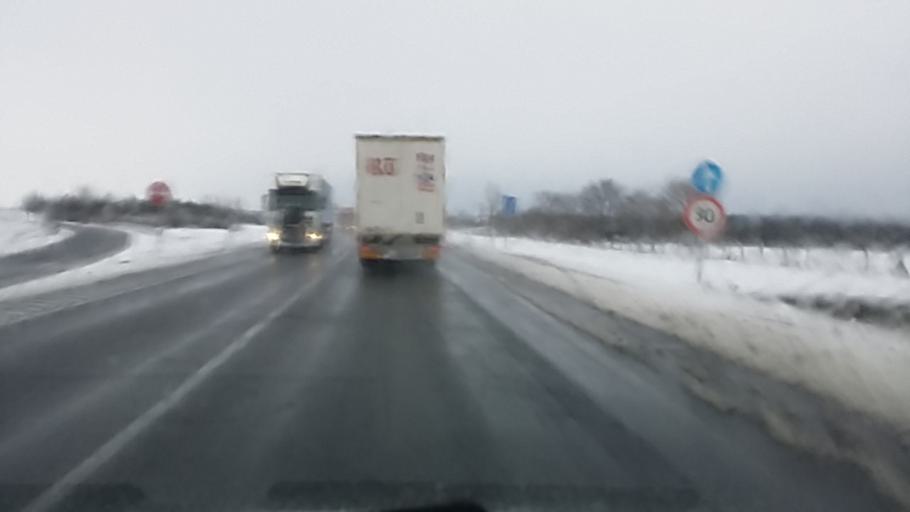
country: HU
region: Gyor-Moson-Sopron
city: Rajka
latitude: 47.9989
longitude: 17.1846
